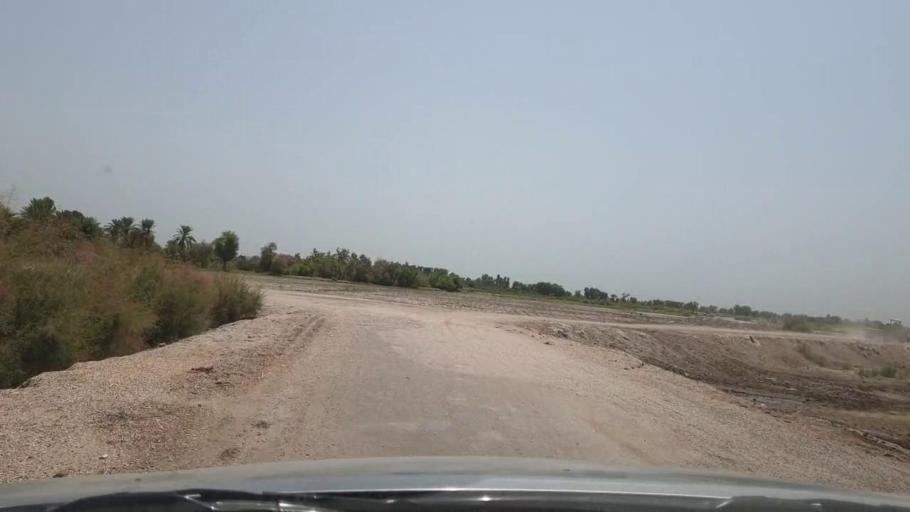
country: PK
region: Sindh
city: Pano Aqil
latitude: 27.8703
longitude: 69.1676
